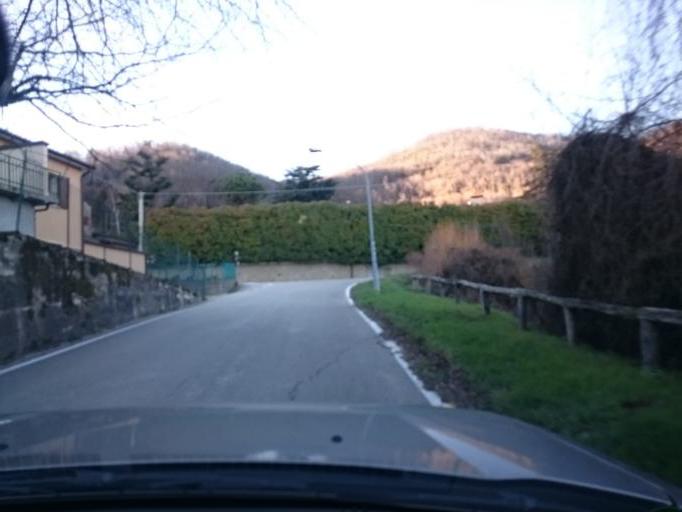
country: IT
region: Veneto
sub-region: Provincia di Padova
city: Bastia
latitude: 45.3530
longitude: 11.6703
